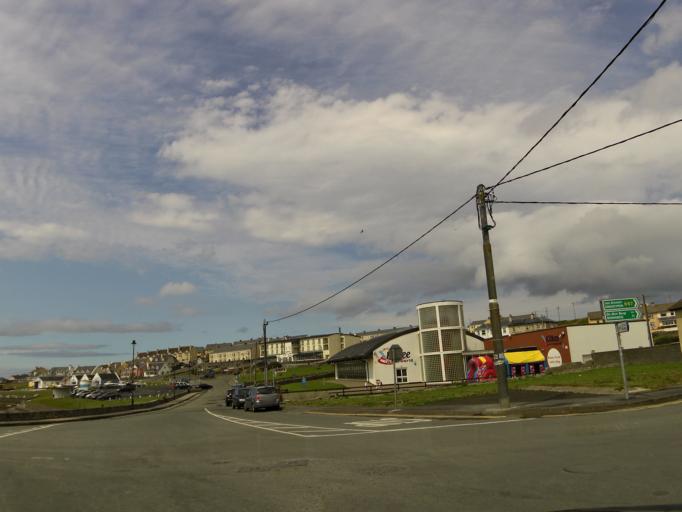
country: IE
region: Munster
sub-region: An Clar
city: Kilrush
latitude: 52.6824
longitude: -9.6459
